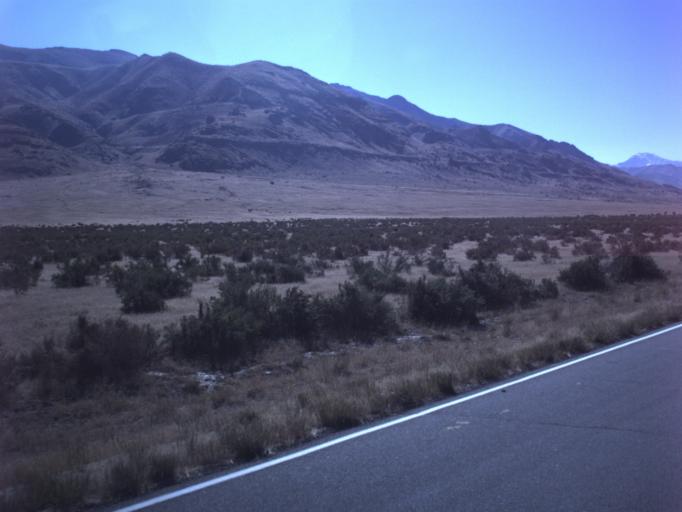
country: US
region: Utah
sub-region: Tooele County
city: Grantsville
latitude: 40.7080
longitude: -112.6637
